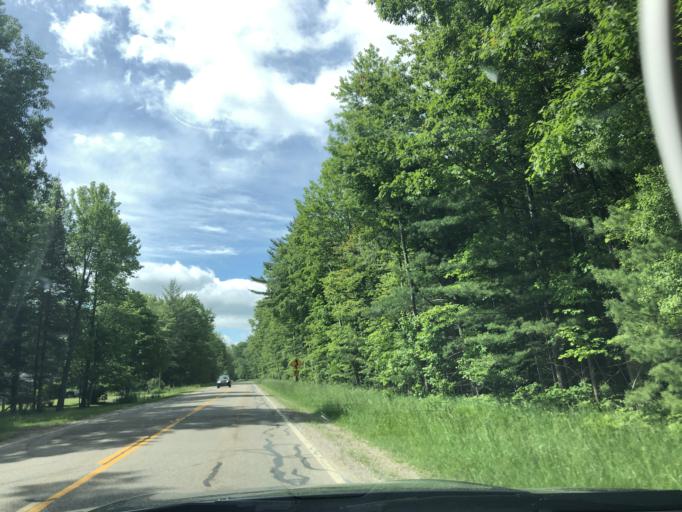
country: US
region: Michigan
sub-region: Roscommon County
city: Houghton Lake
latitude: 44.3550
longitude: -84.8549
